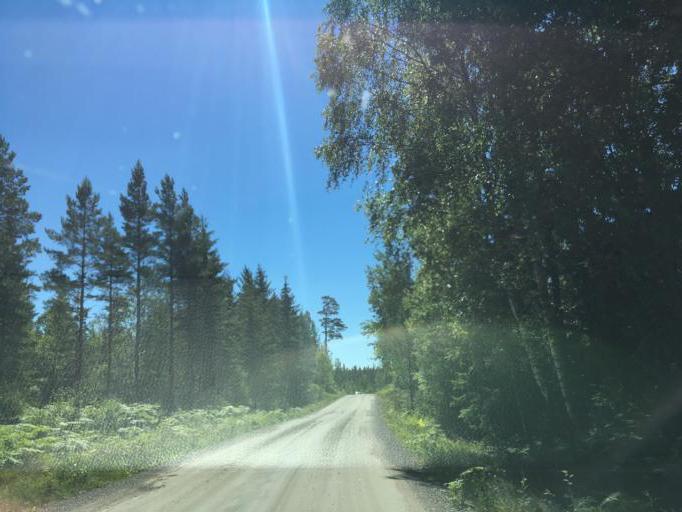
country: SE
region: Vaestra Goetaland
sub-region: Karlsborgs Kommun
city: Karlsborg
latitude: 58.7426
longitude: 14.5839
